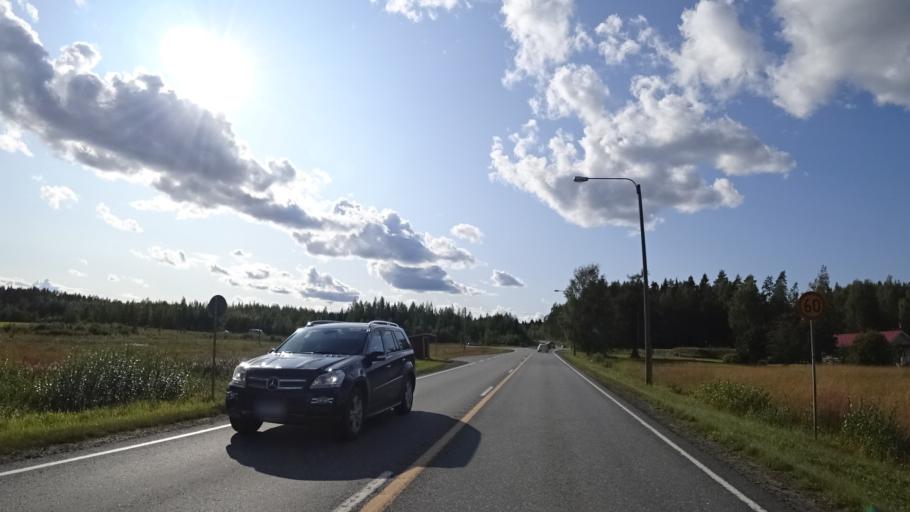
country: FI
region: North Karelia
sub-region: Keski-Karjala
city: Kitee
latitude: 62.0914
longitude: 29.9616
